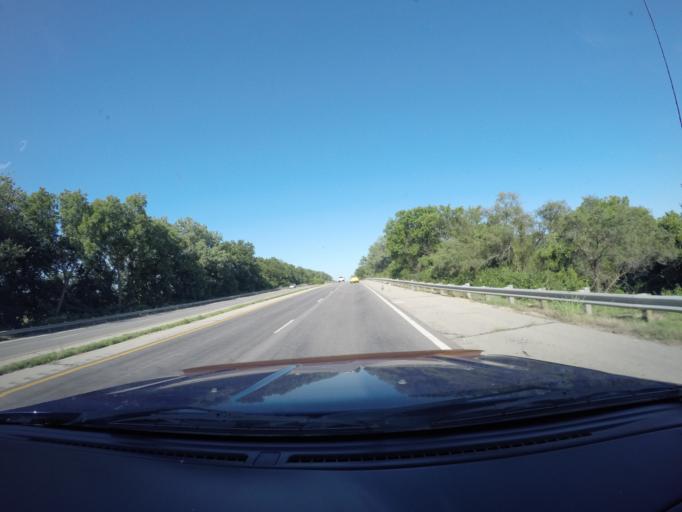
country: US
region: Kansas
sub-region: Shawnee County
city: Topeka
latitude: 39.0910
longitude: -95.6377
